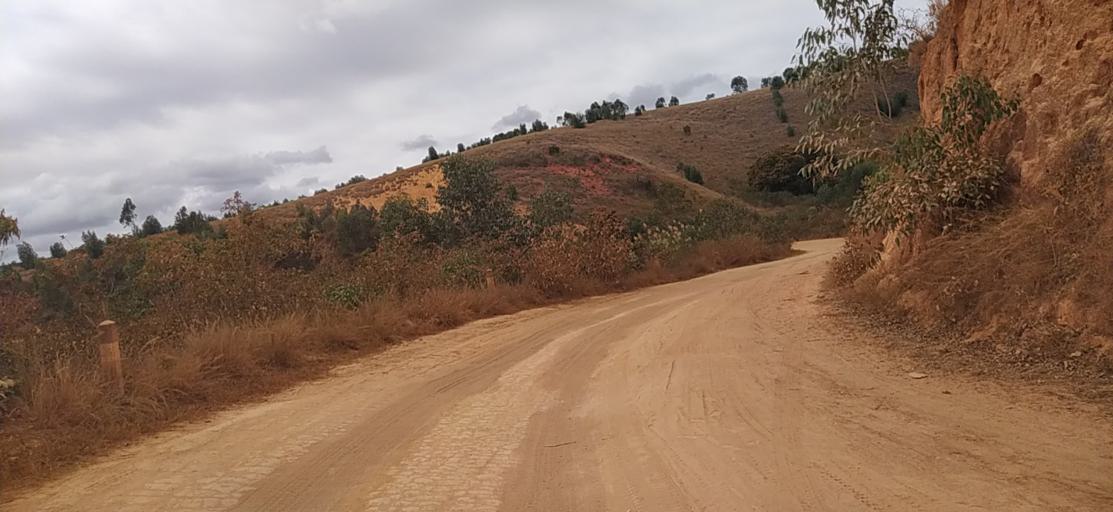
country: MG
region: Alaotra Mangoro
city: Ambatondrazaka
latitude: -18.0013
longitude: 48.2627
